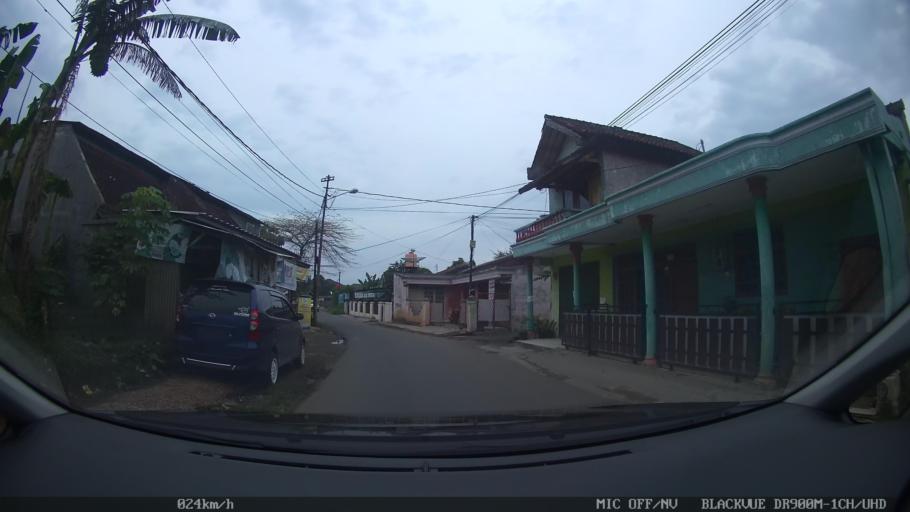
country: ID
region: Lampung
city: Kedaton
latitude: -5.3820
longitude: 105.2500
